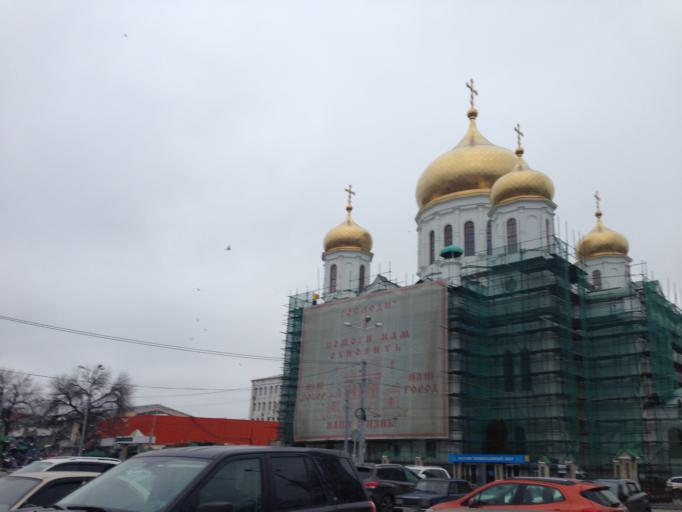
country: RU
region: Rostov
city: Rostov-na-Donu
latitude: 47.2178
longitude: 39.7112
